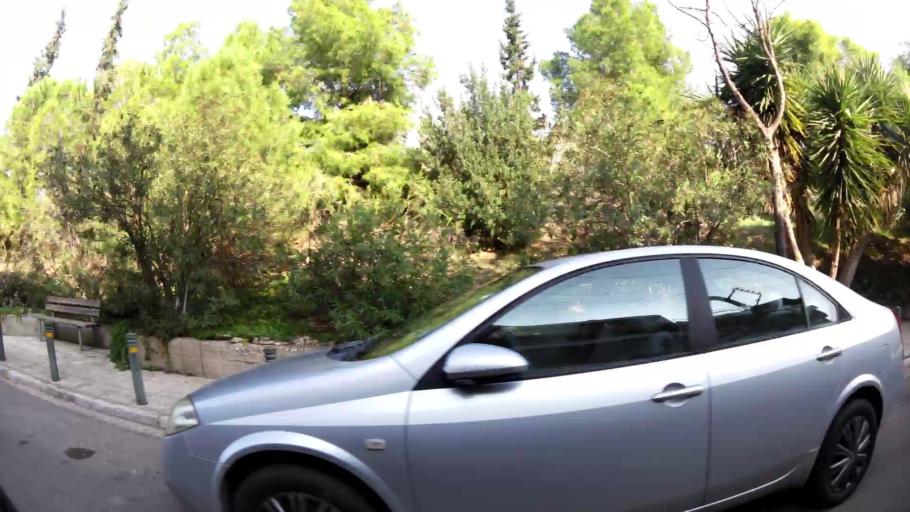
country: GR
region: Attica
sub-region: Nomarchia Athinas
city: Argyroupoli
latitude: 37.9119
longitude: 23.7577
